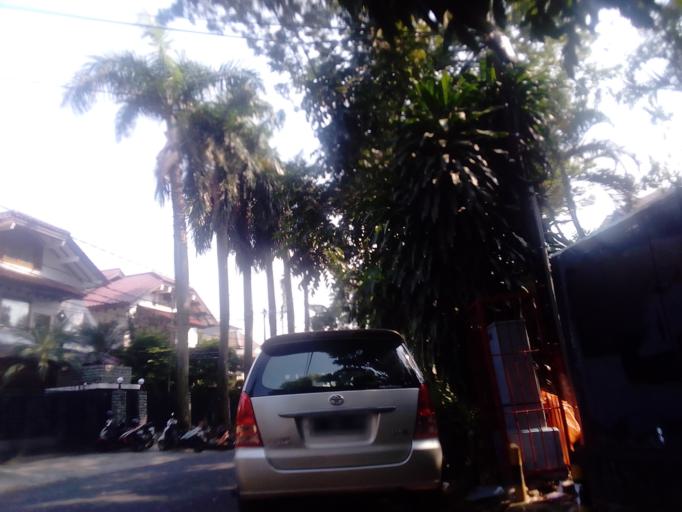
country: ID
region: Jakarta Raya
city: Jakarta
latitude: -6.2561
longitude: 106.8020
